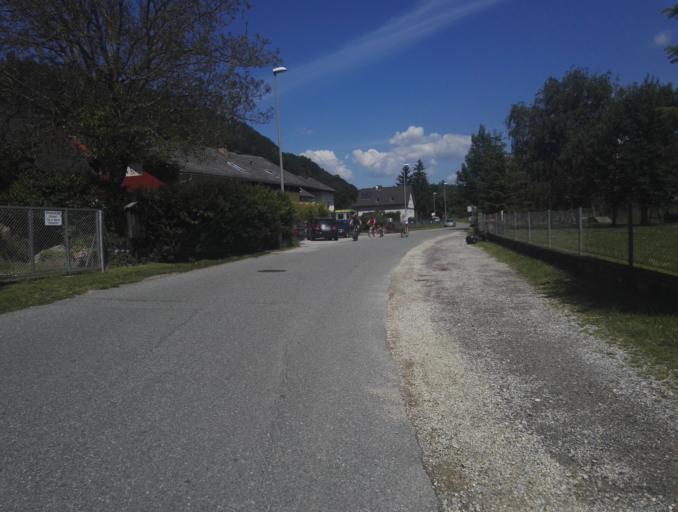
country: AT
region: Styria
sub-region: Graz Stadt
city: Goesting
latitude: 47.1113
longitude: 15.3739
